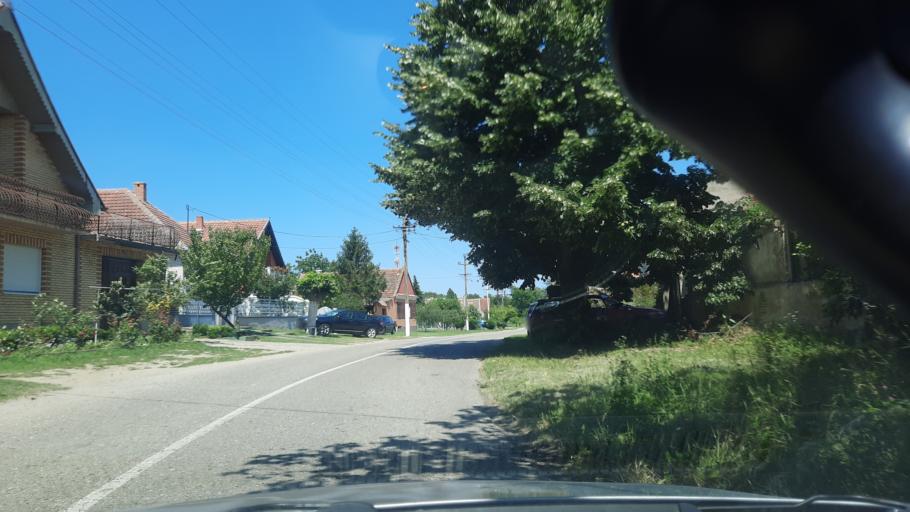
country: RO
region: Caras-Severin
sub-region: Comuna Socol
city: Socol
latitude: 44.8479
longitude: 21.3359
